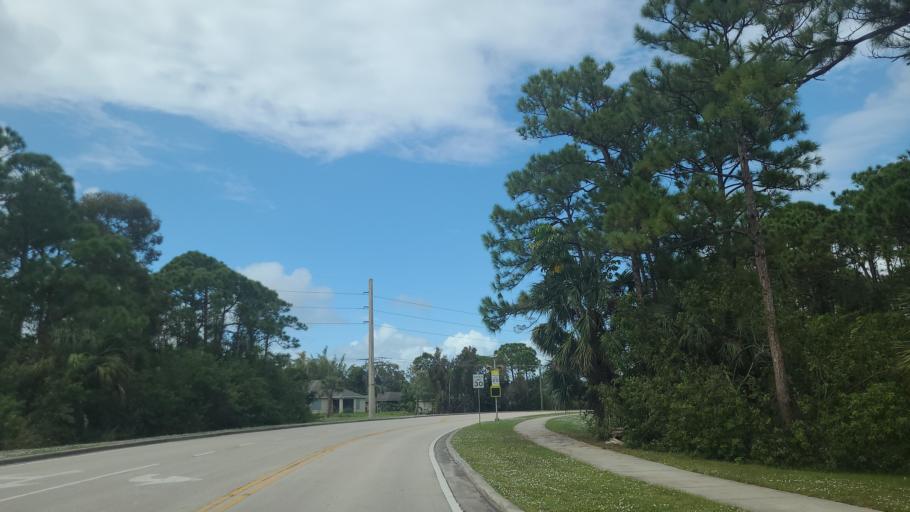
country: US
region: Florida
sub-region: Indian River County
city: Sebastian
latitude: 27.8018
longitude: -80.4775
